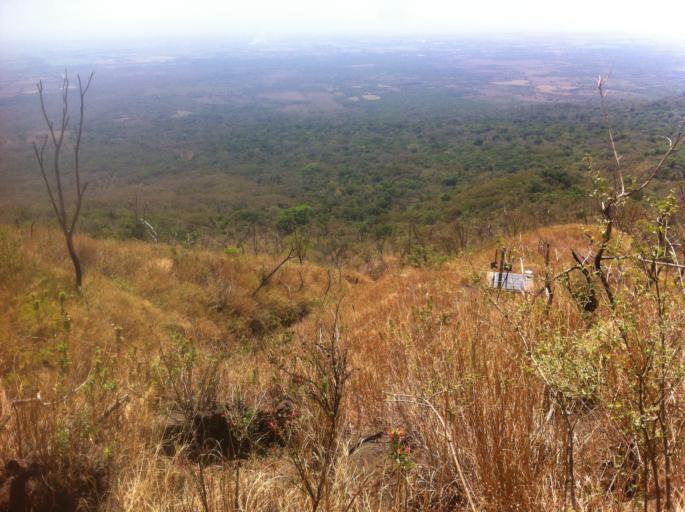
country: NI
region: Chinandega
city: Chichigalpa
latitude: 12.6968
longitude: -87.0206
